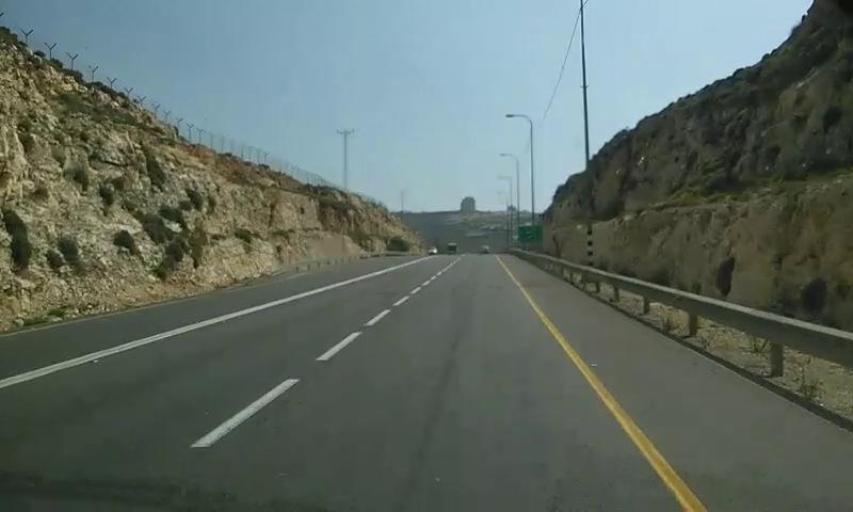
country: PS
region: West Bank
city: Jaba`
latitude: 31.8667
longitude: 35.2587
